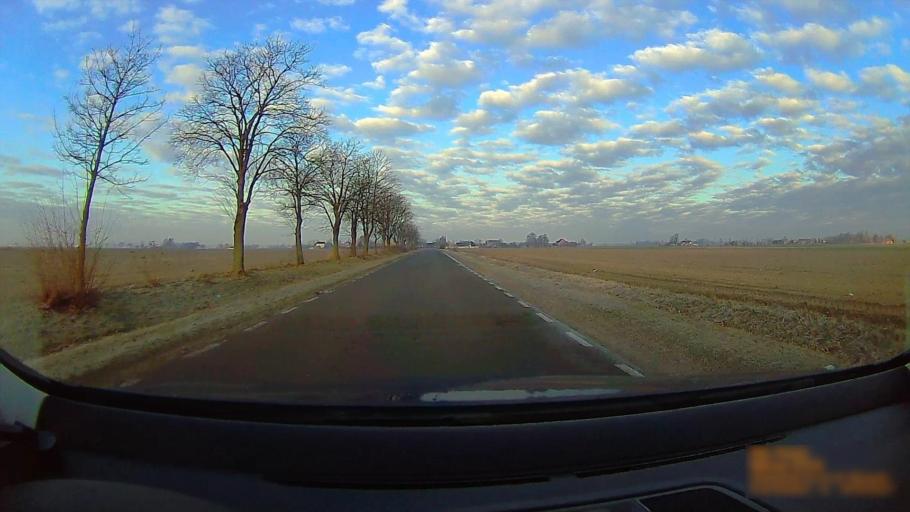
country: PL
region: Greater Poland Voivodeship
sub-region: Powiat koninski
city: Rychwal
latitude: 52.0972
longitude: 18.1261
